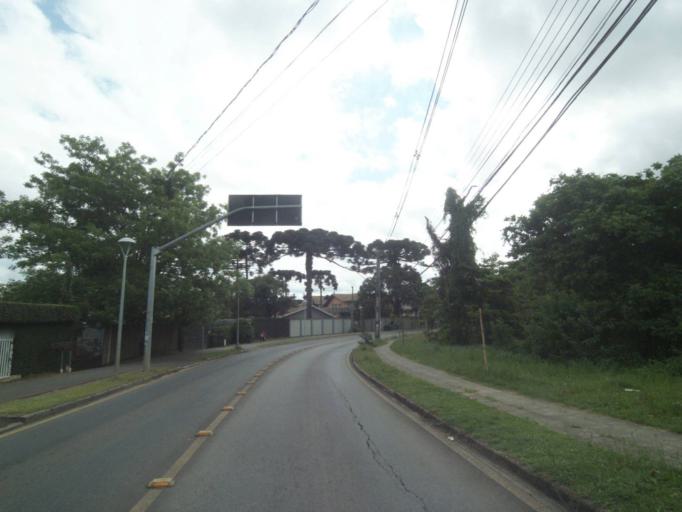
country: BR
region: Parana
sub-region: Curitiba
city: Curitiba
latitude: -25.3838
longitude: -49.2889
